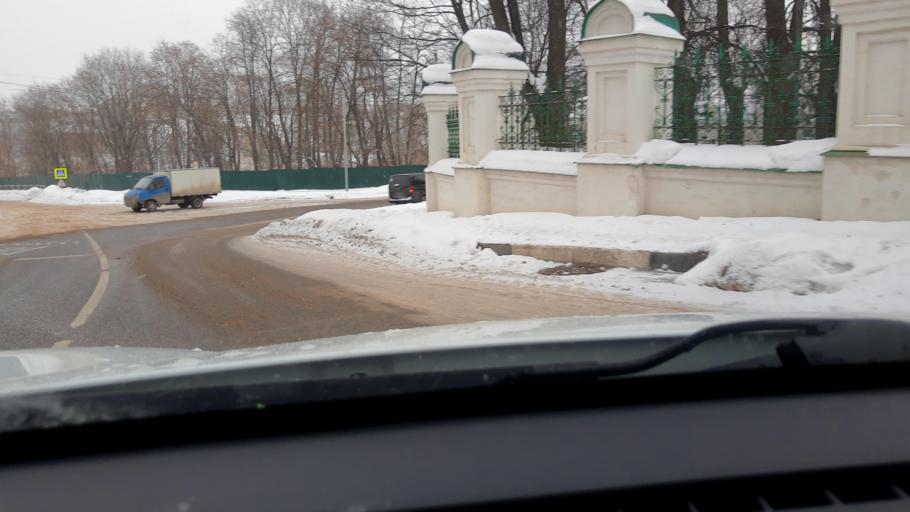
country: RU
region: Moskovskaya
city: Pavlovskaya Sloboda
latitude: 55.8152
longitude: 37.0904
